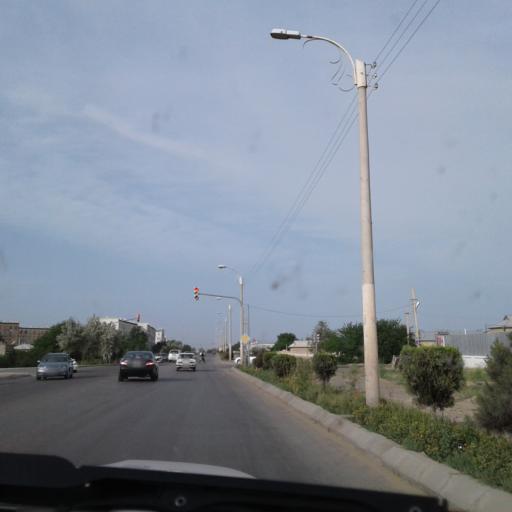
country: TM
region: Mary
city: Mary
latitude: 37.5799
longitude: 61.8711
